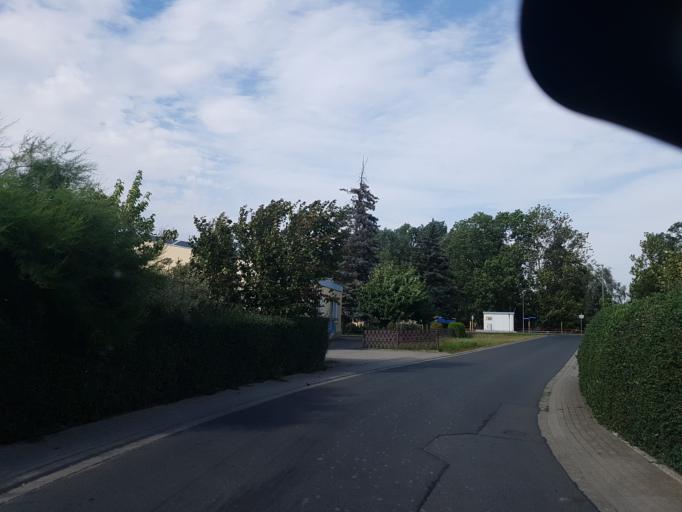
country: DE
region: Saxony
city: Ostrau
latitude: 51.2238
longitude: 13.1799
